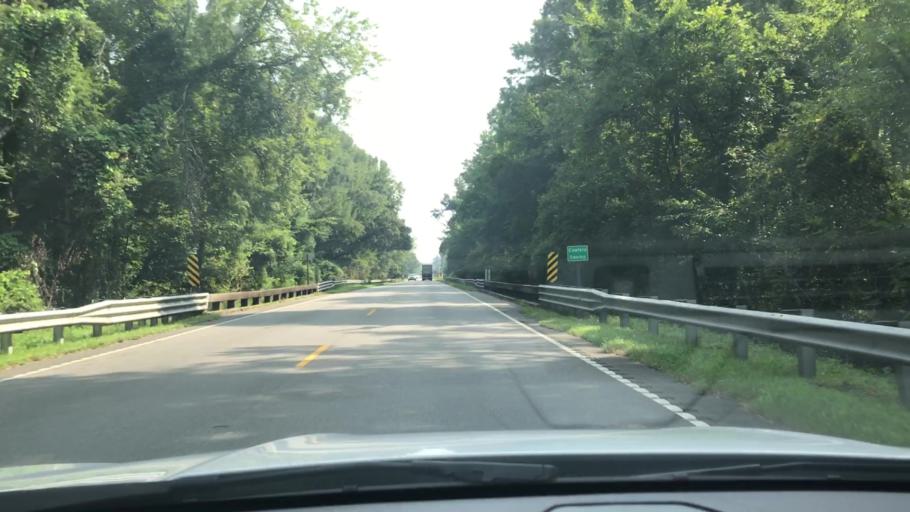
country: US
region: South Carolina
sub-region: Horry County
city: Socastee
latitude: 33.6866
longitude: -79.1217
